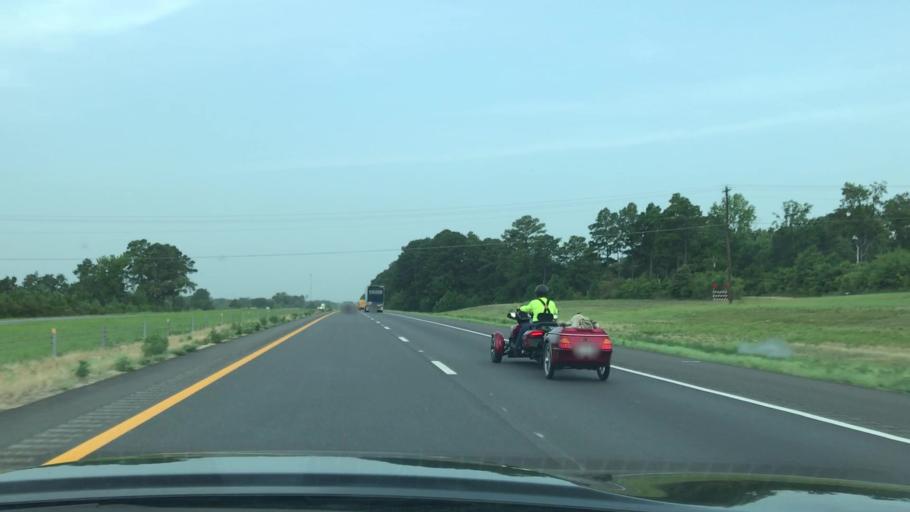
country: US
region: Texas
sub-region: Harrison County
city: Hallsville
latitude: 32.4666
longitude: -94.6230
